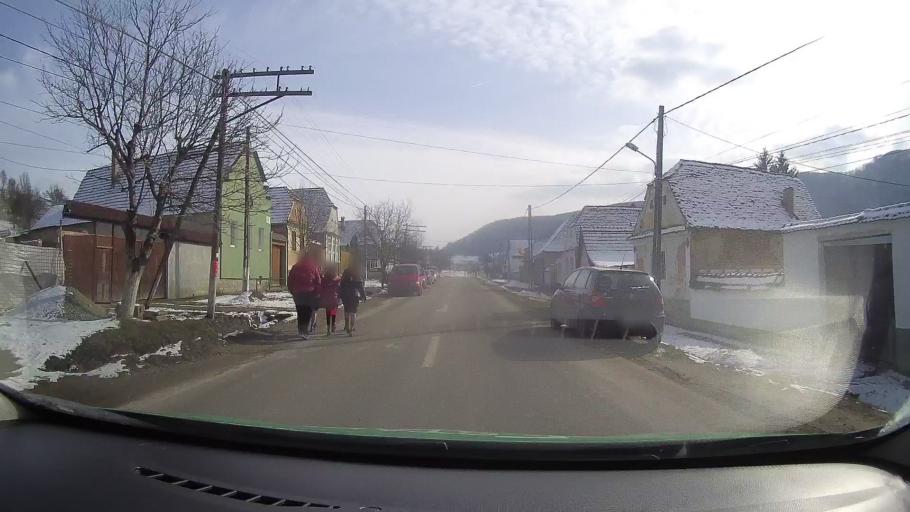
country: RO
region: Mures
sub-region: Comuna Apold
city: Saes
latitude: 46.1537
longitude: 24.7701
